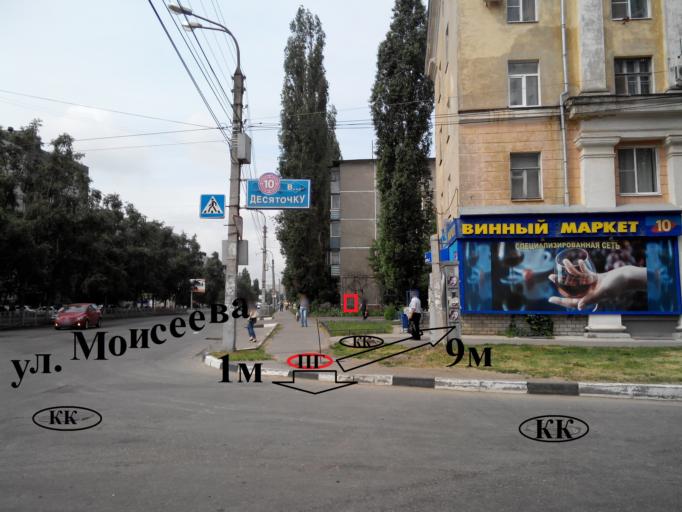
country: RU
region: Voronezj
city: Voronezh
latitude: 51.6521
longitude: 39.1788
